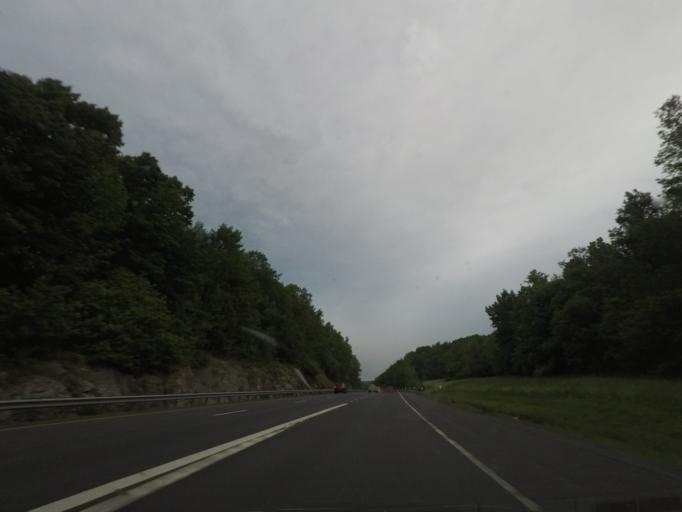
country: US
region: New York
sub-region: Columbia County
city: Chatham
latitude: 42.4253
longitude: -73.5507
